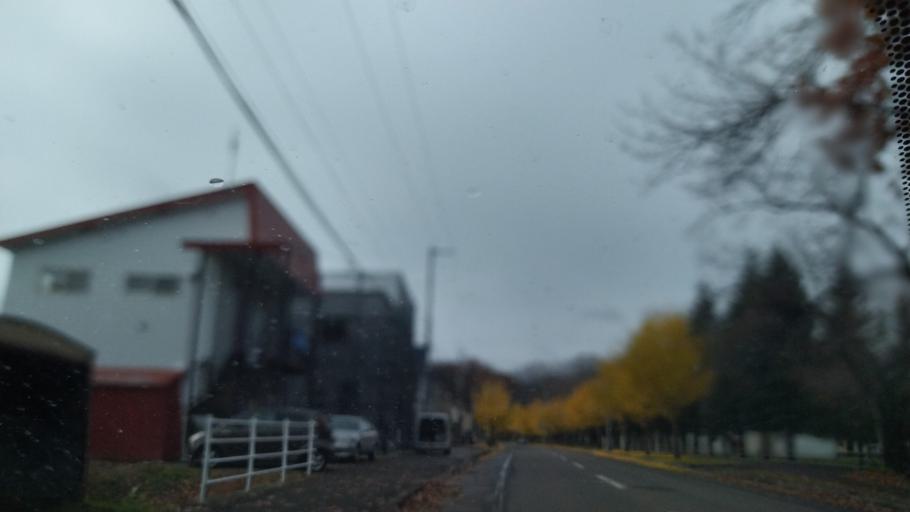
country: JP
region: Hokkaido
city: Obihiro
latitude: 42.8858
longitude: 143.1893
